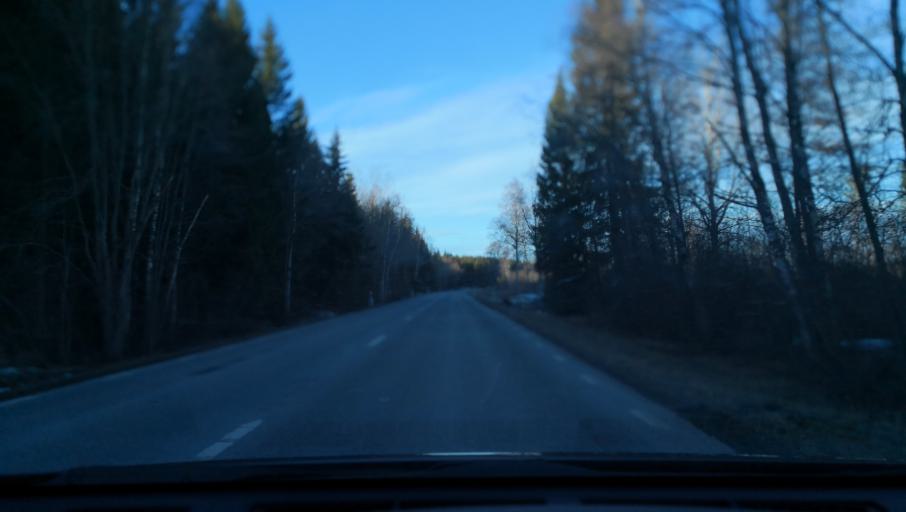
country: SE
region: Uppsala
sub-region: Osthammars Kommun
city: Gimo
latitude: 60.1887
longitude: 18.1900
